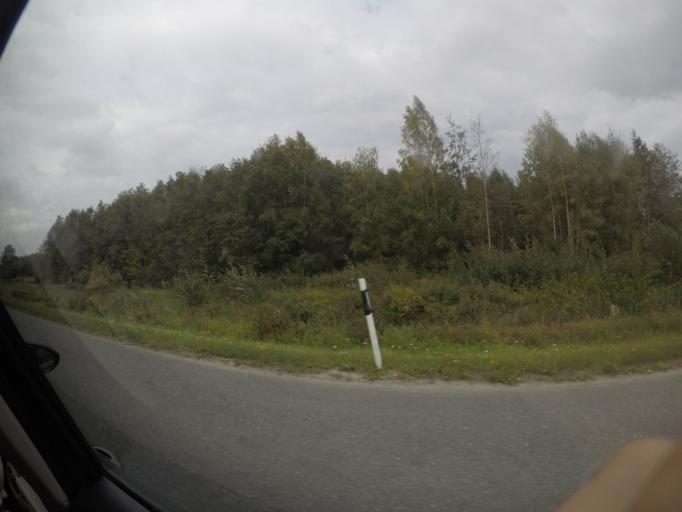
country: FI
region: Haeme
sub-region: Haemeenlinna
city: Parola
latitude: 61.0374
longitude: 24.4067
